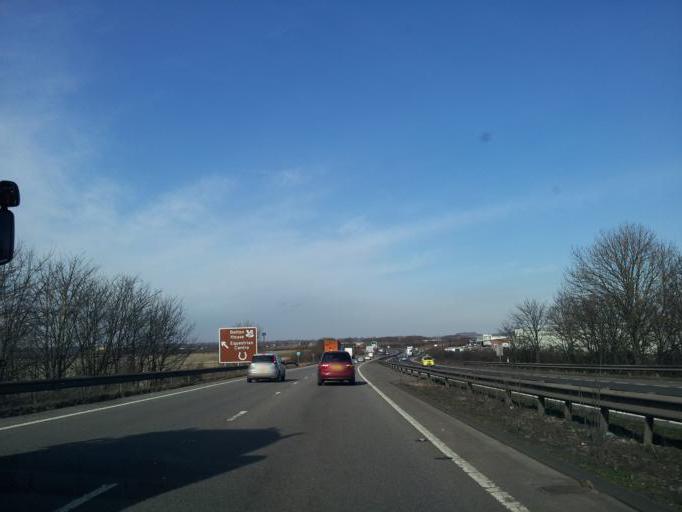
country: GB
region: England
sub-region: Lincolnshire
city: Great Gonerby
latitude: 52.9407
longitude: -0.6848
